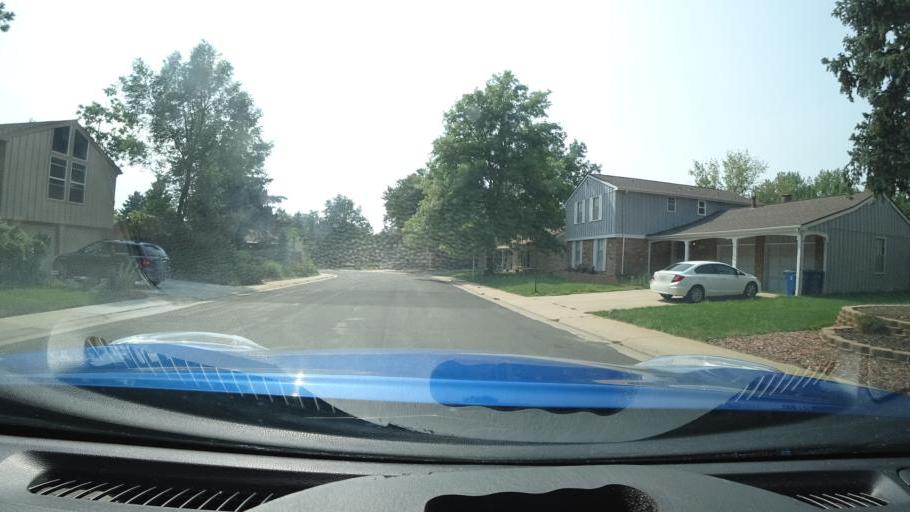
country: US
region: Colorado
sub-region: Adams County
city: Aurora
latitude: 39.6671
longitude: -104.8553
